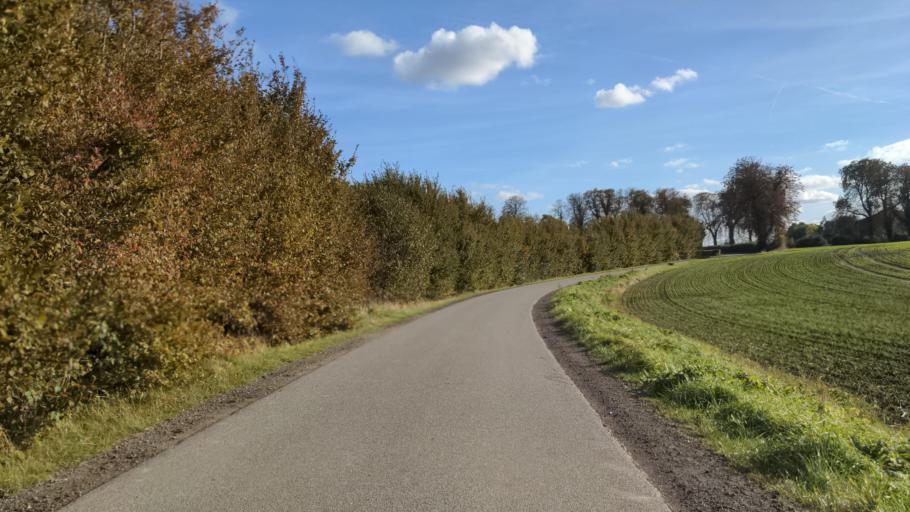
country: DE
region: Schleswig-Holstein
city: Manhagen
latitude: 54.1862
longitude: 10.9095
